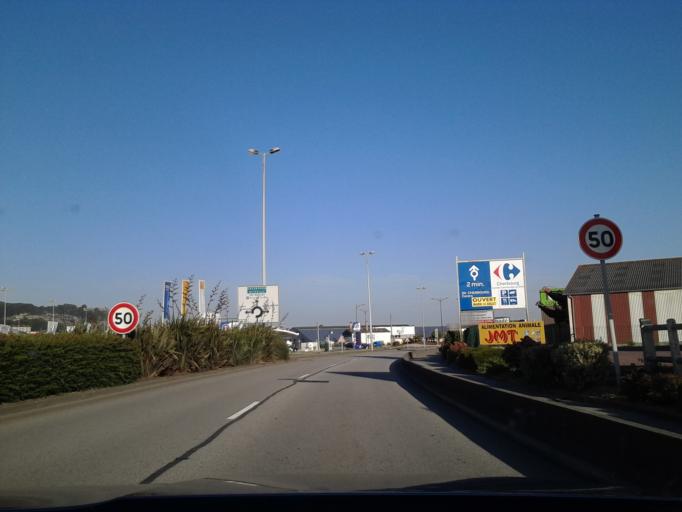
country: FR
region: Lower Normandy
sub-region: Departement de la Manche
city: Tourlaville
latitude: 49.6349
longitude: -1.5890
